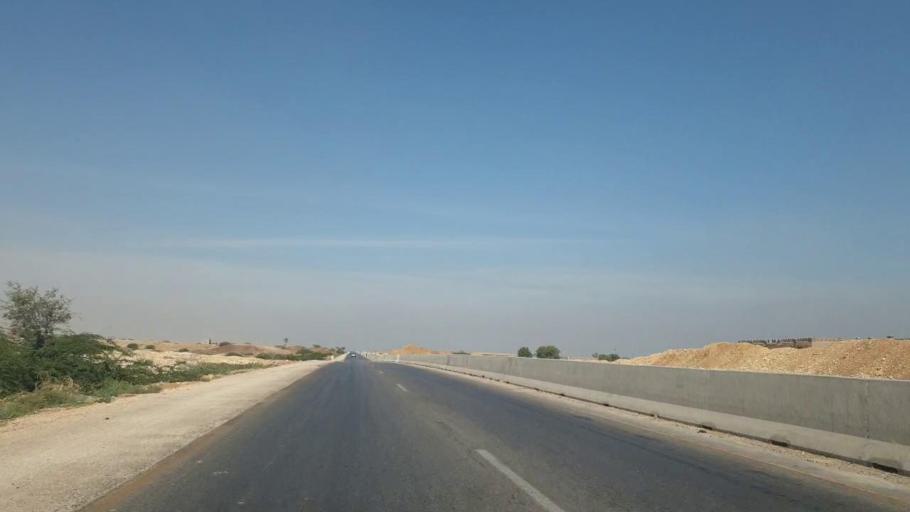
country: PK
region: Sindh
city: Matiari
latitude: 25.6727
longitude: 68.2958
